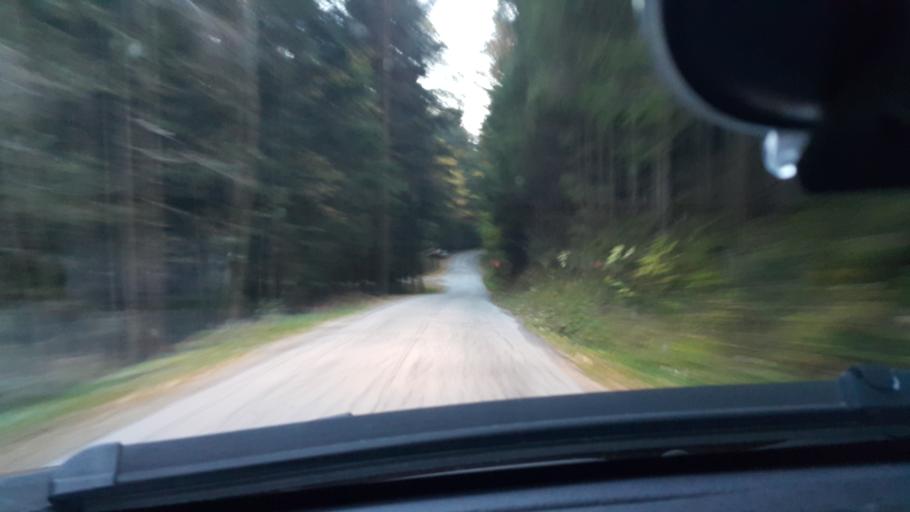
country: SI
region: Mislinja
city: Mislinja
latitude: 46.4229
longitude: 15.2730
